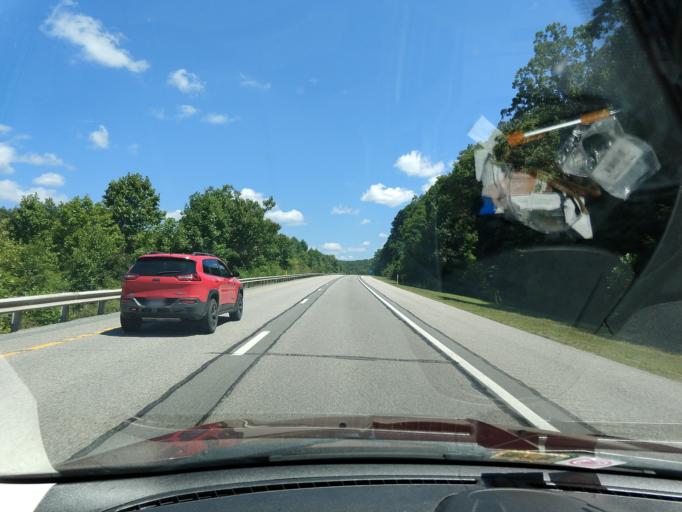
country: US
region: West Virginia
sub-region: Fayette County
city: Ansted
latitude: 38.0974
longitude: -81.0352
